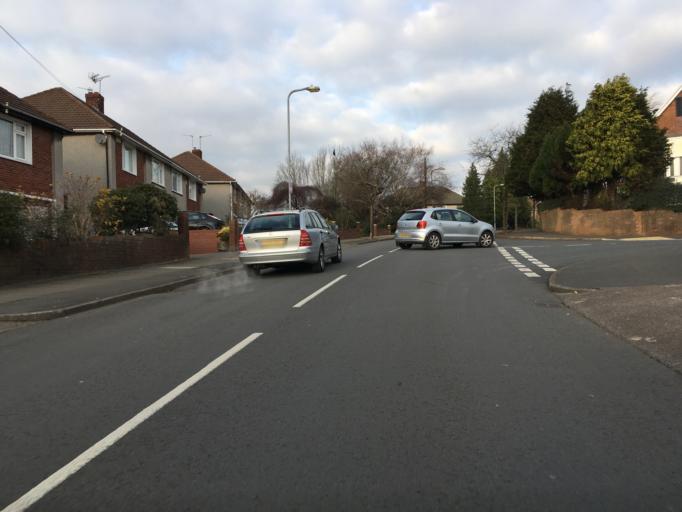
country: GB
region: Wales
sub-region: Cardiff
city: Cardiff
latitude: 51.5044
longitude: -3.1716
